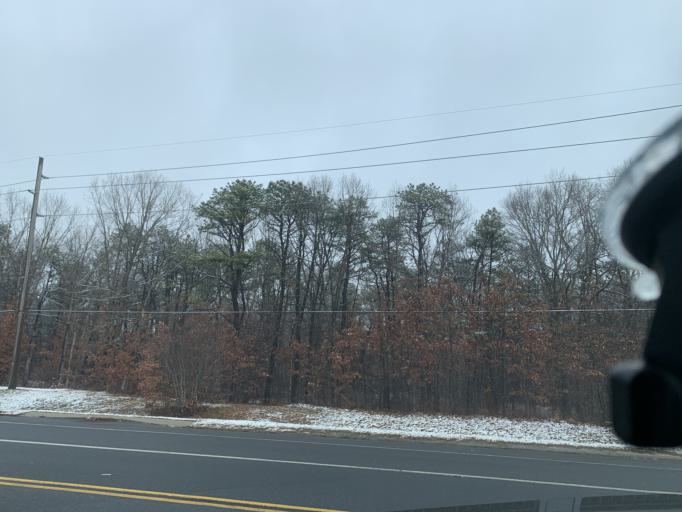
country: US
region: New Jersey
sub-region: Atlantic County
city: Pomona
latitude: 39.4325
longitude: -74.5819
